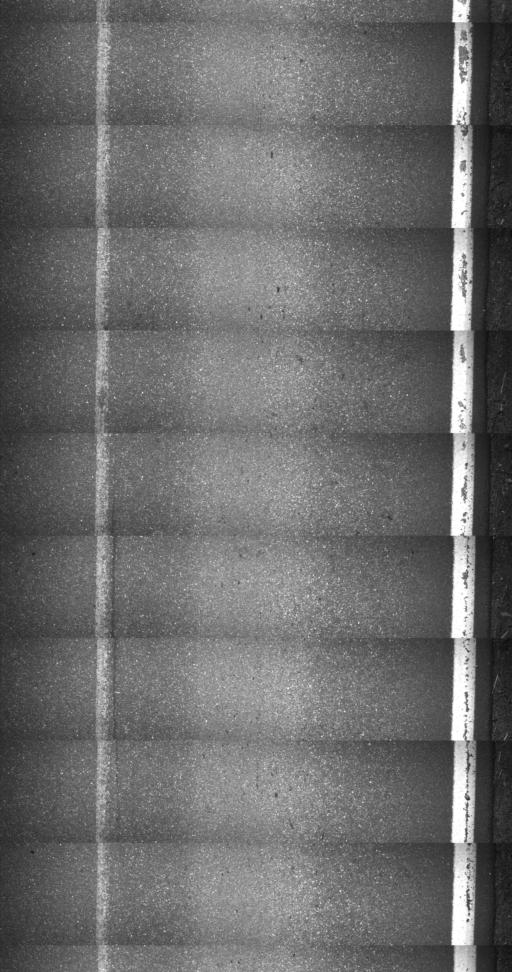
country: US
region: Vermont
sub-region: Orange County
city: Chelsea
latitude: 43.9272
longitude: -72.4655
